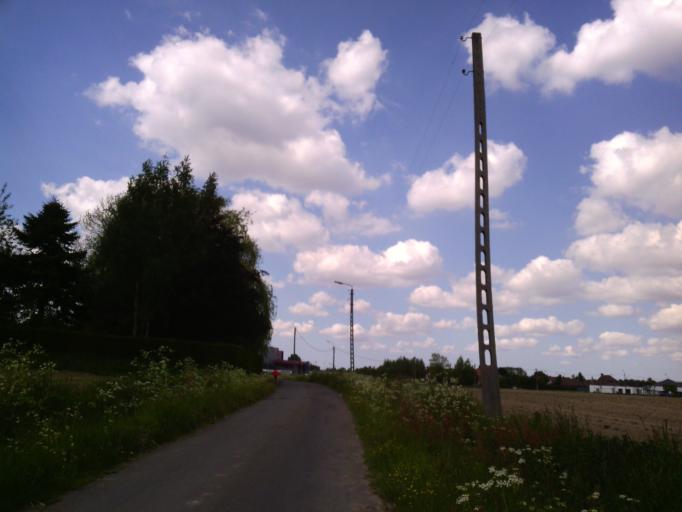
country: BE
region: Flanders
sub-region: Provincie West-Vlaanderen
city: Wevelgem
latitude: 50.7862
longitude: 3.1530
